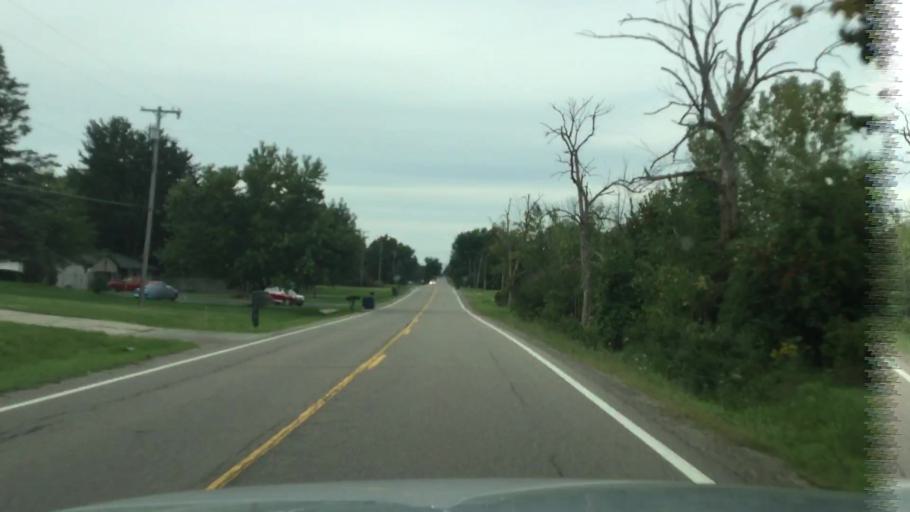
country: US
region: Michigan
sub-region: Genesee County
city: Linden
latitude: 42.8721
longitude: -83.7686
